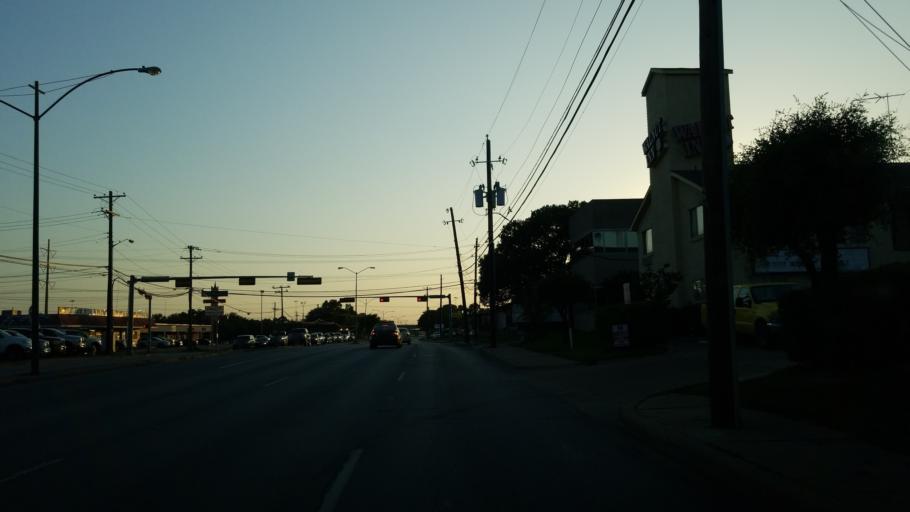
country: US
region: Texas
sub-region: Dallas County
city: Farmers Branch
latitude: 32.8812
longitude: -96.8895
